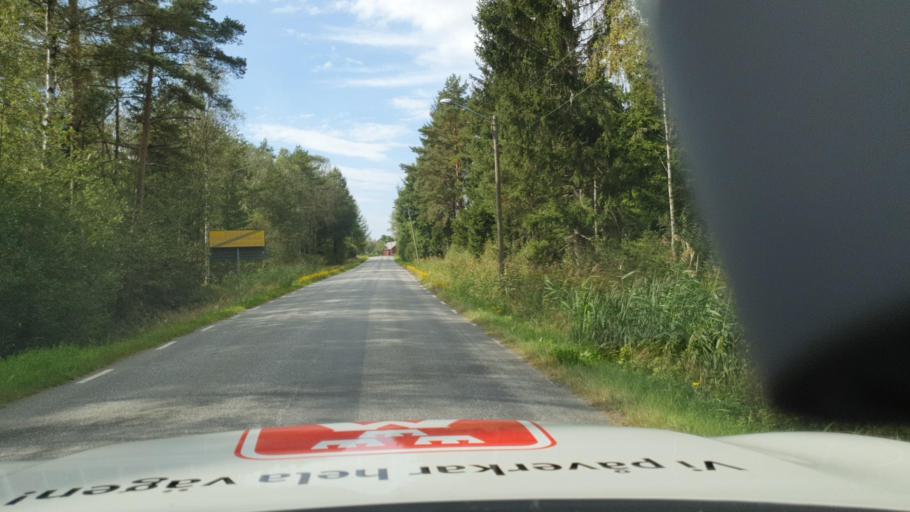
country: SE
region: Vaestra Goetaland
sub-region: Marks Kommun
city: Kinna
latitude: 57.3939
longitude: 12.7991
